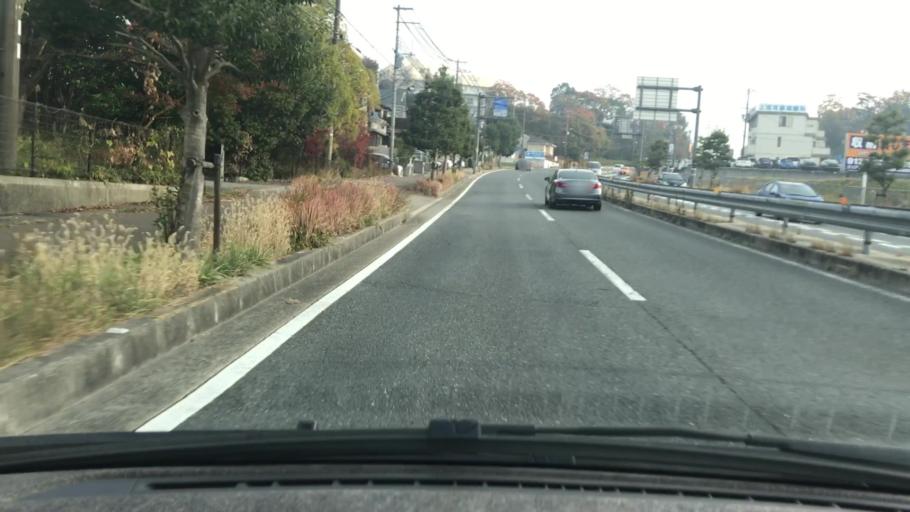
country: JP
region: Hyogo
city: Sandacho
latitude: 34.8302
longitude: 135.2514
